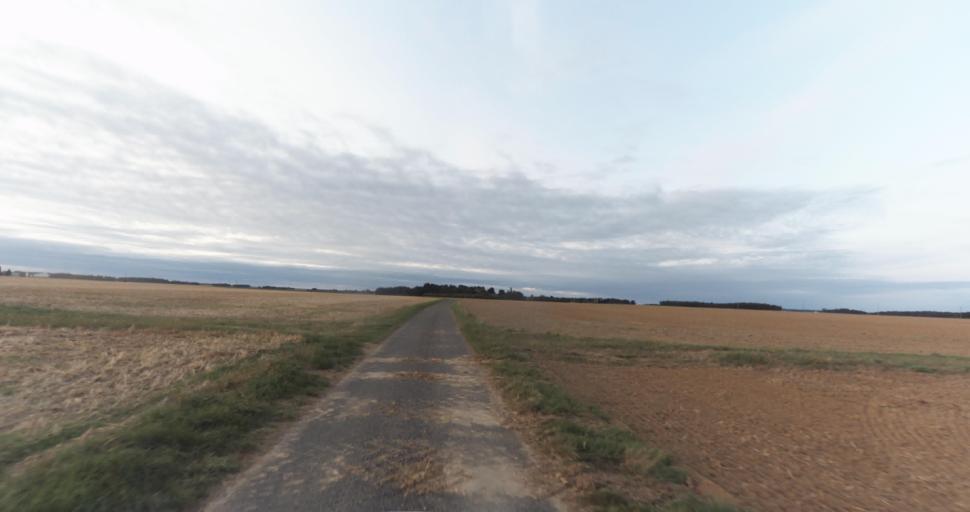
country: FR
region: Haute-Normandie
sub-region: Departement de l'Eure
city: La Madeleine-de-Nonancourt
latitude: 48.8719
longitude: 1.2307
